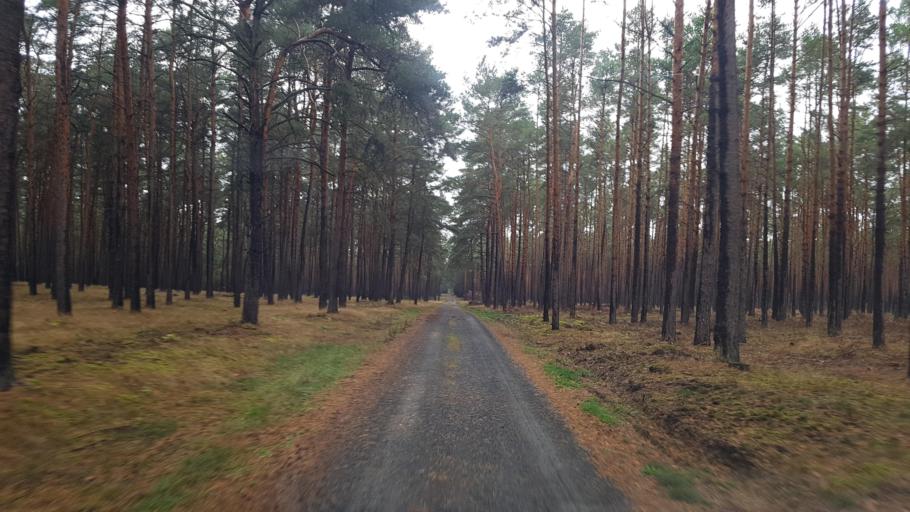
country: DE
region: Brandenburg
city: Schlieben
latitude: 51.7382
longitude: 13.3465
